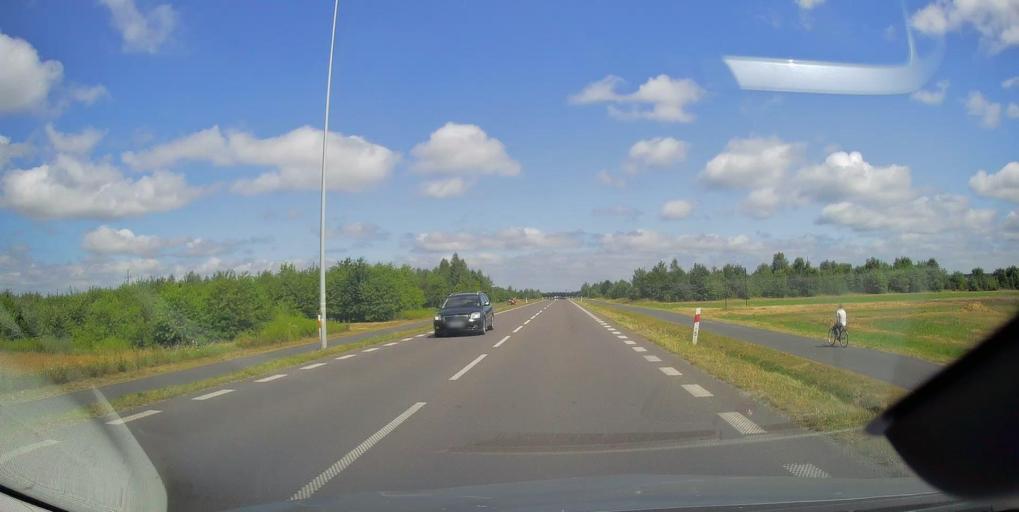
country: PL
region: Subcarpathian Voivodeship
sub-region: Powiat mielecki
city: Mielec
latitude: 50.3319
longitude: 21.4885
